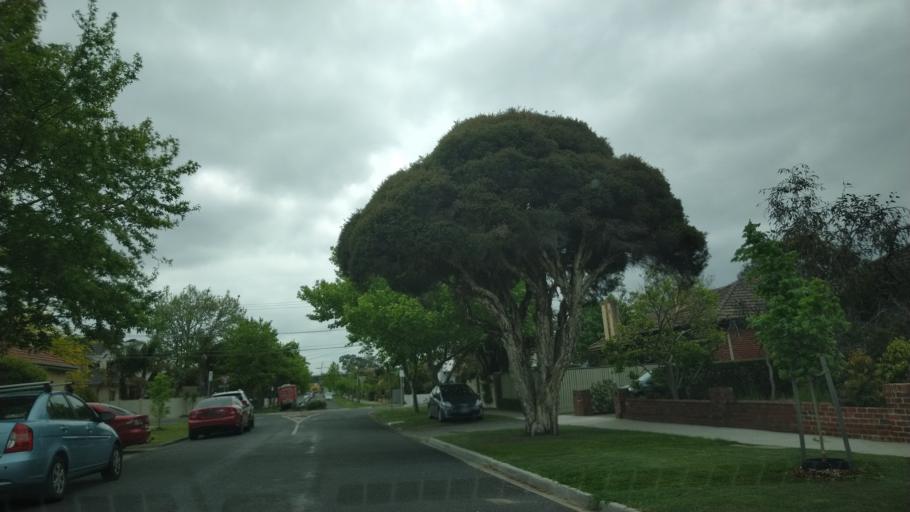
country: AU
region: Victoria
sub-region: Glen Eira
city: Murrumbeena
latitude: -37.8946
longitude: 145.0681
